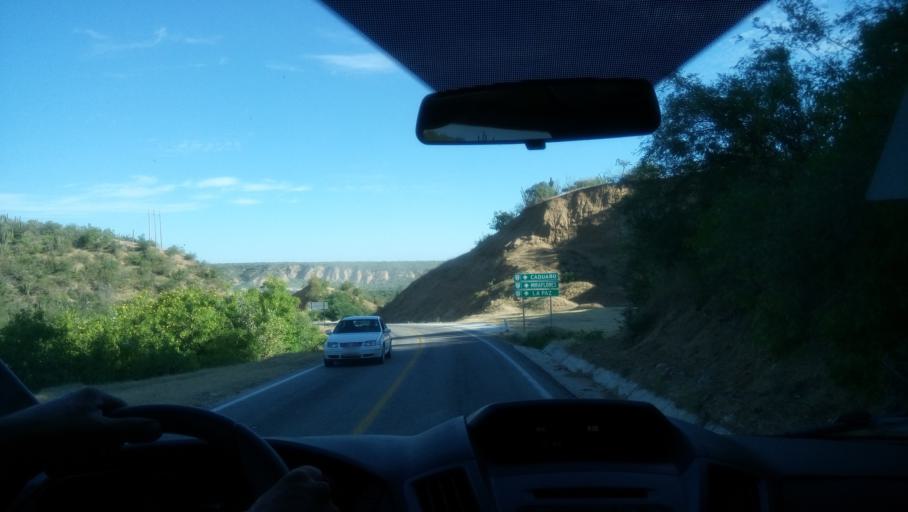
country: MX
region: Baja California Sur
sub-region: Los Cabos
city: Las Veredas
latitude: 23.3263
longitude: -109.7634
